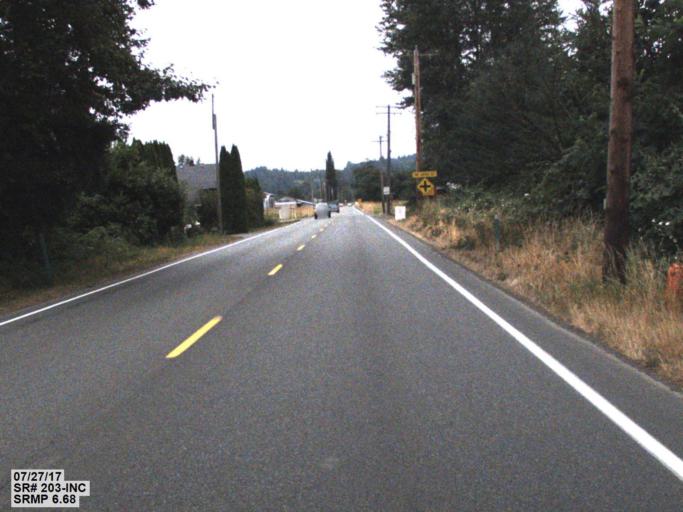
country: US
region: Washington
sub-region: King County
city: Carnation
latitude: 47.6578
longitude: -121.9106
